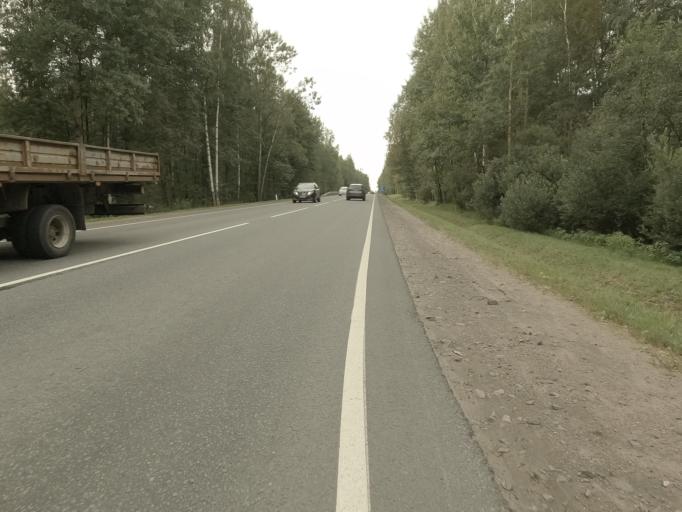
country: RU
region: Leningrad
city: Kirovsk
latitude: 59.8464
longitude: 31.0390
